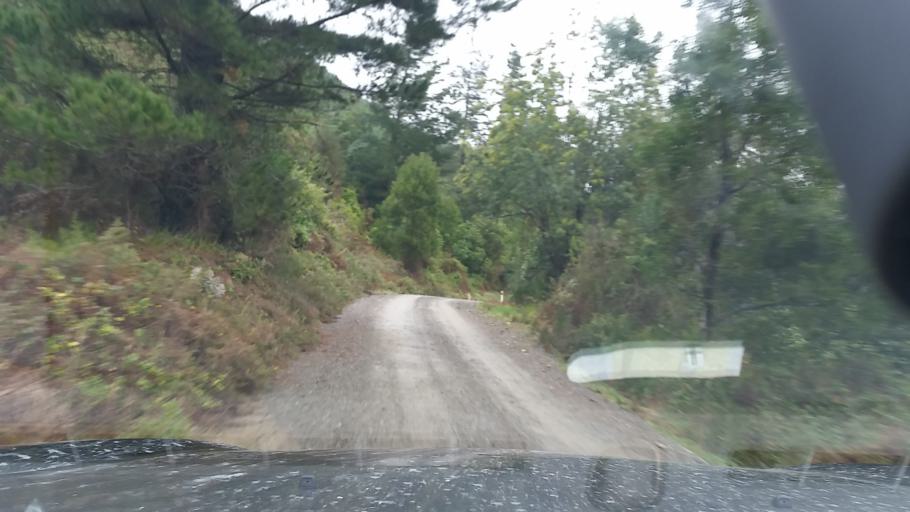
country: NZ
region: Nelson
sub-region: Nelson City
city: Nelson
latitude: -41.3588
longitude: 173.6203
